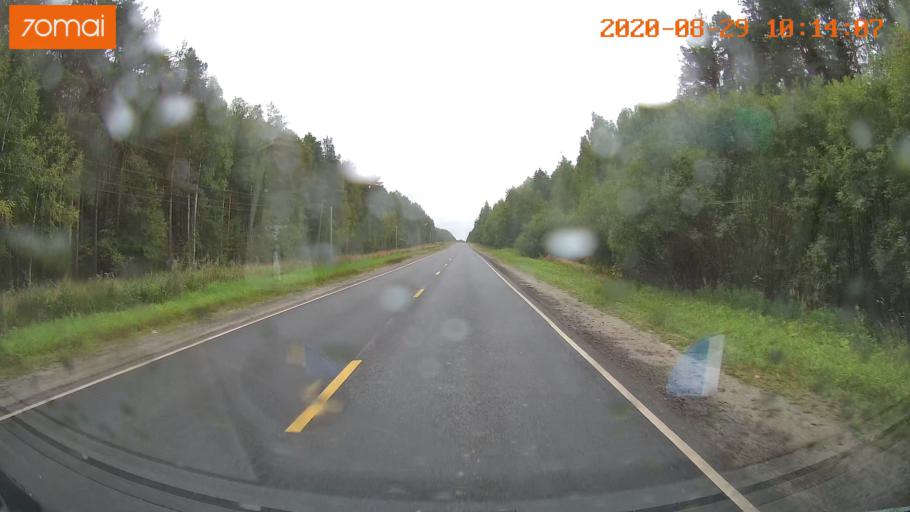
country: RU
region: Ivanovo
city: Yur'yevets
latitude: 57.3562
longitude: 42.7468
